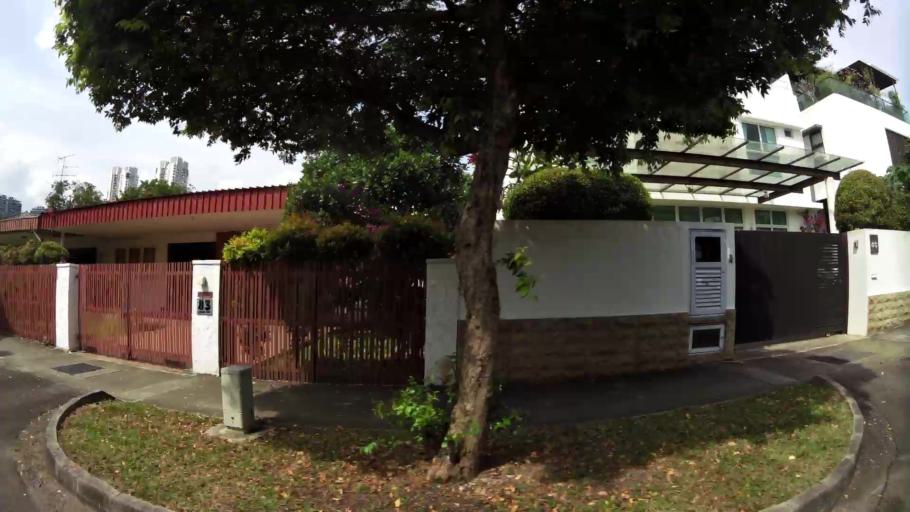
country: SG
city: Singapore
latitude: 1.3250
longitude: 103.7657
